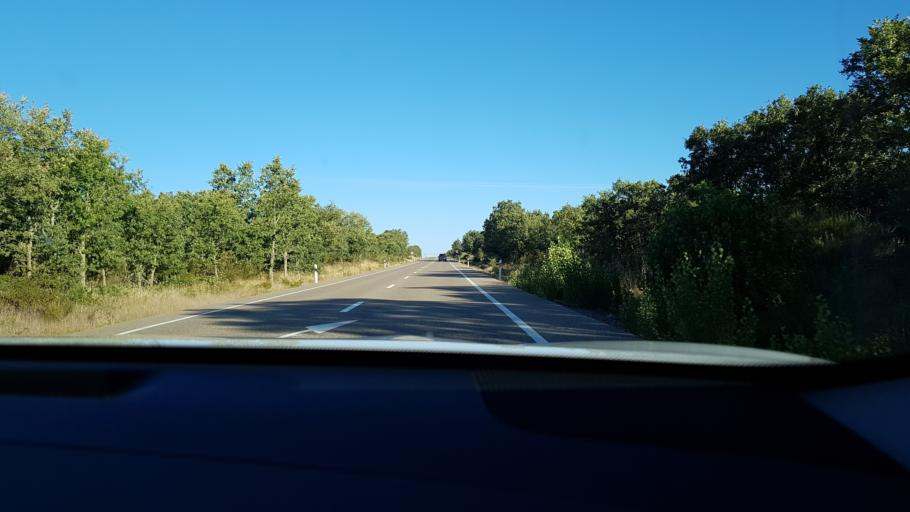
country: ES
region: Castille and Leon
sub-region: Provincia de Zamora
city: Samir de los Canos
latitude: 41.6738
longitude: -6.2374
